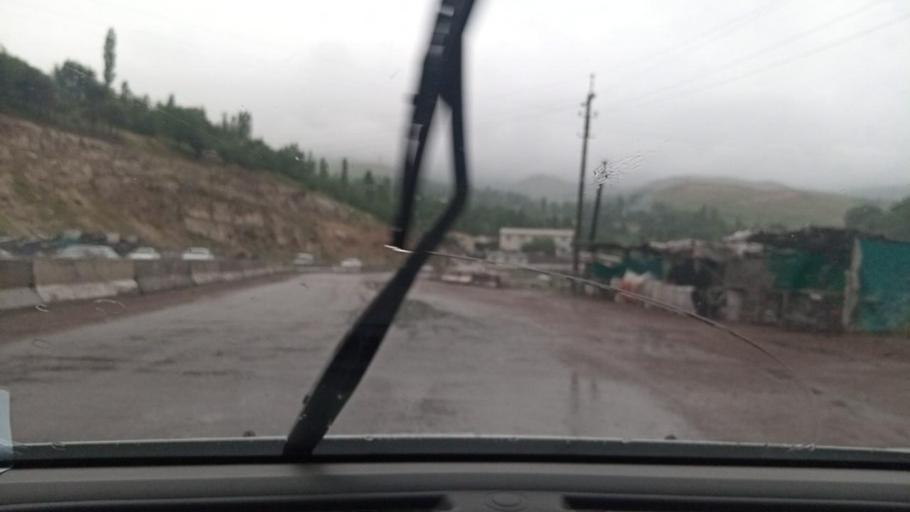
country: UZ
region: Toshkent
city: Angren
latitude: 41.0729
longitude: 70.2519
